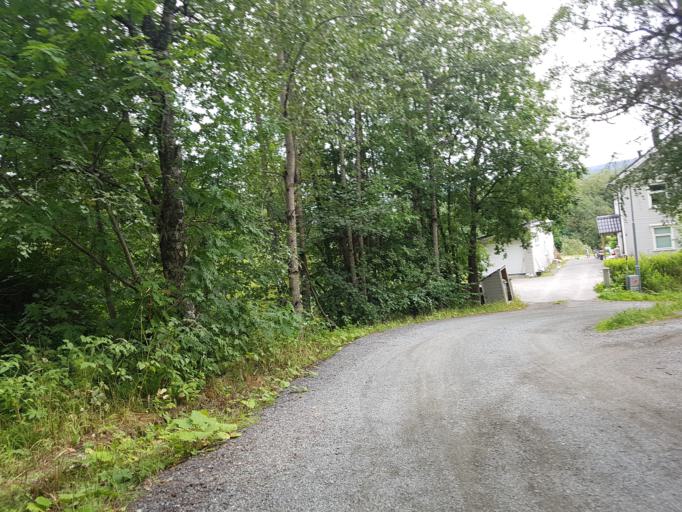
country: NO
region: Sor-Trondelag
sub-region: Trondheim
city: Trondheim
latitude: 63.3892
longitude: 10.3762
